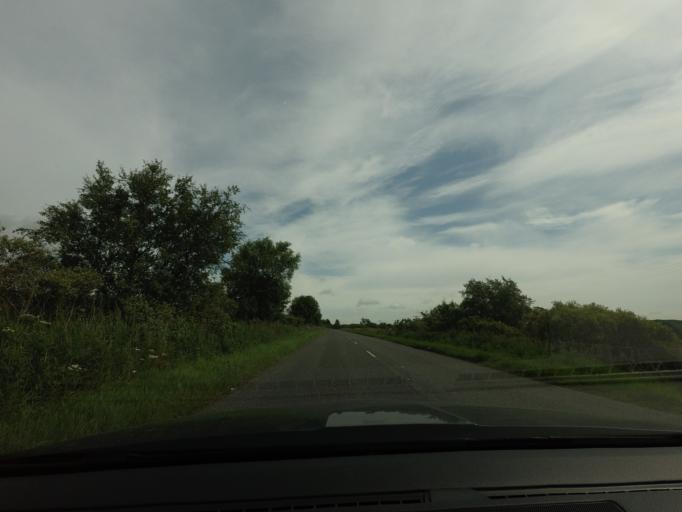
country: GB
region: Scotland
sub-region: Aberdeenshire
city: Turriff
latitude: 57.5962
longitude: -2.2944
